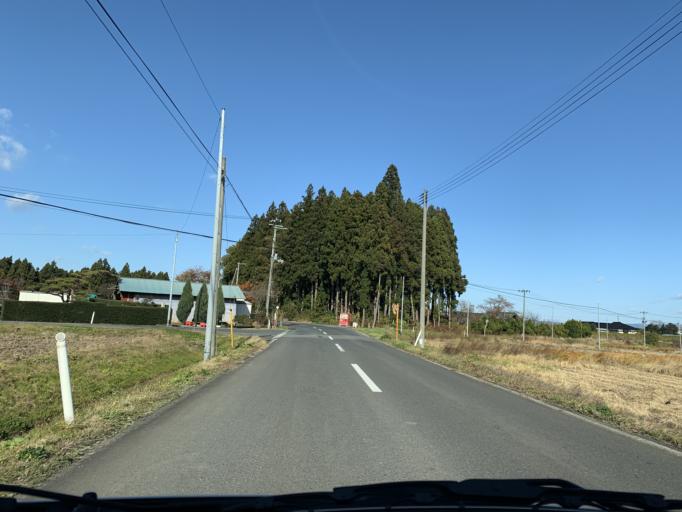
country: JP
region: Iwate
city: Mizusawa
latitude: 39.0790
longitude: 141.1212
